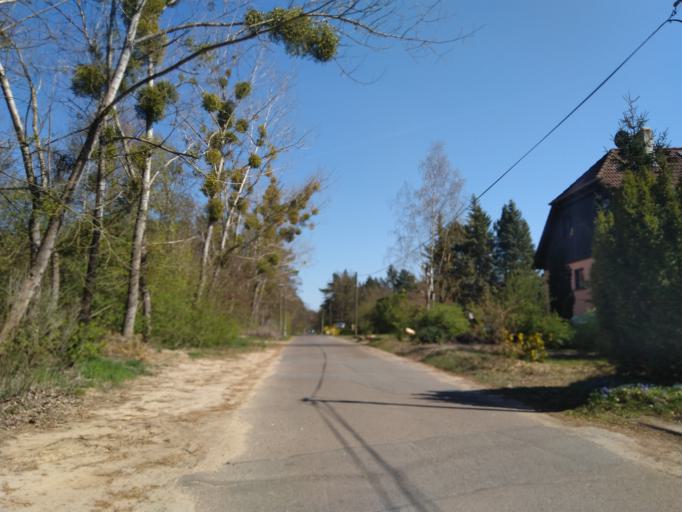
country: DE
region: Brandenburg
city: Biesenthal
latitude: 52.7781
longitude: 13.6048
